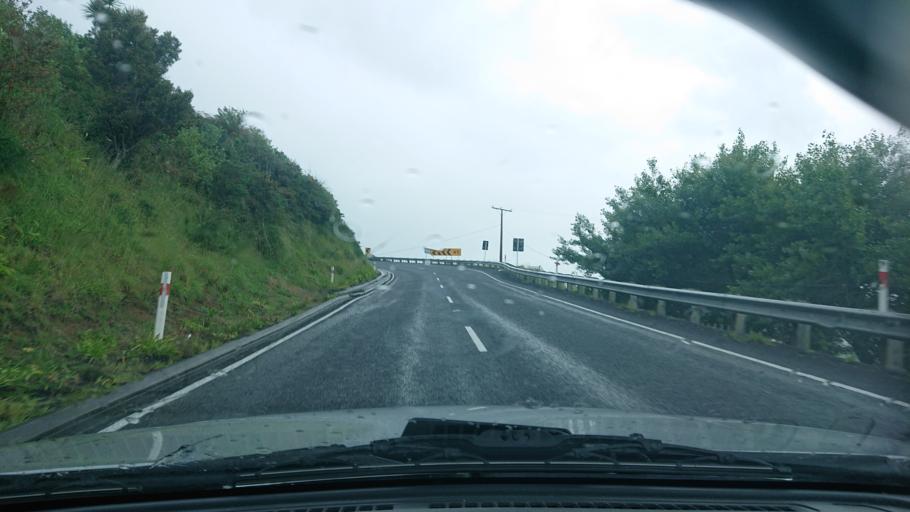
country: NZ
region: Auckland
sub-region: Auckland
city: Wellsford
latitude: -36.3468
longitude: 174.4746
